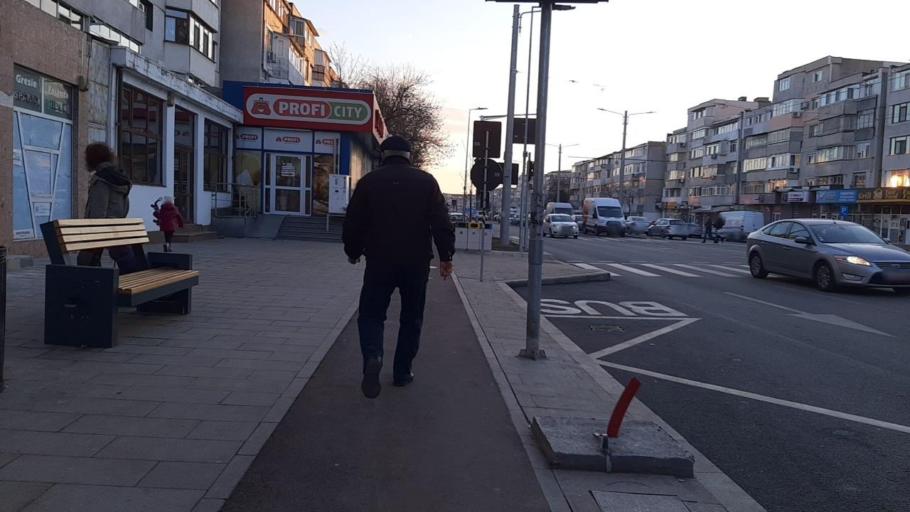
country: RO
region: Galati
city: Galati
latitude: 45.4450
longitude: 28.0233
